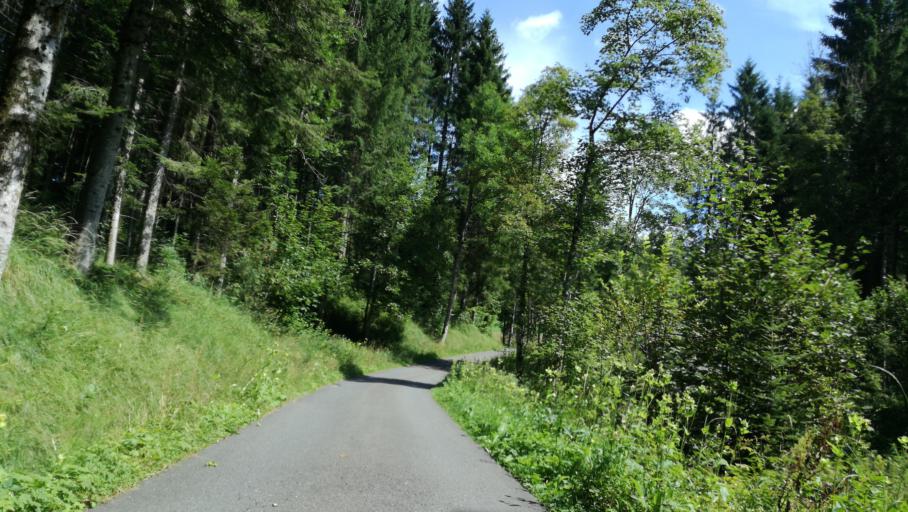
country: CH
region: Schwyz
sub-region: Bezirk Schwyz
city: Rothenthurm
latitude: 47.1360
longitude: 8.6564
